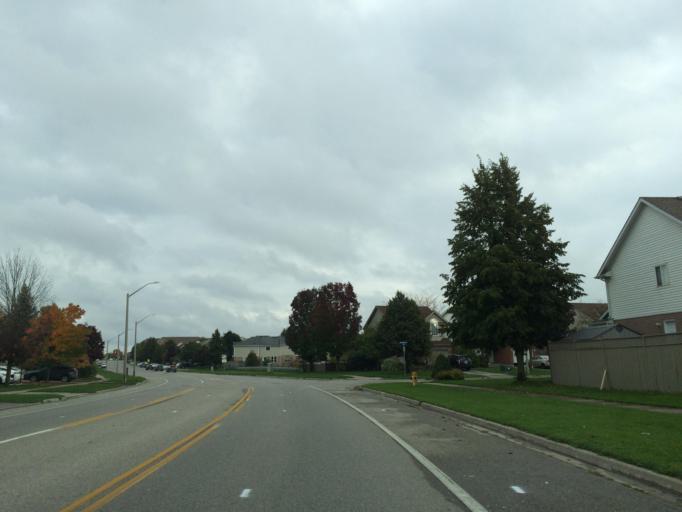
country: CA
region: Ontario
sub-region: Wellington County
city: Guelph
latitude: 43.5674
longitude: -80.2279
